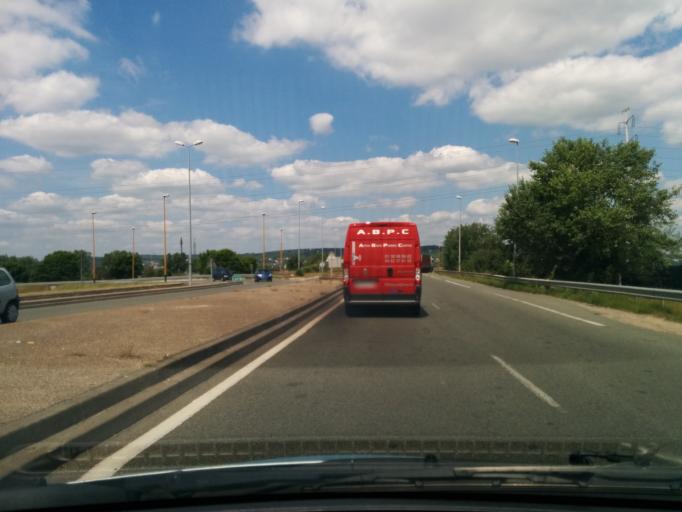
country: FR
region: Ile-de-France
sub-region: Departement des Yvelines
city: Flins-sur-Seine
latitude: 48.9672
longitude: 1.8652
